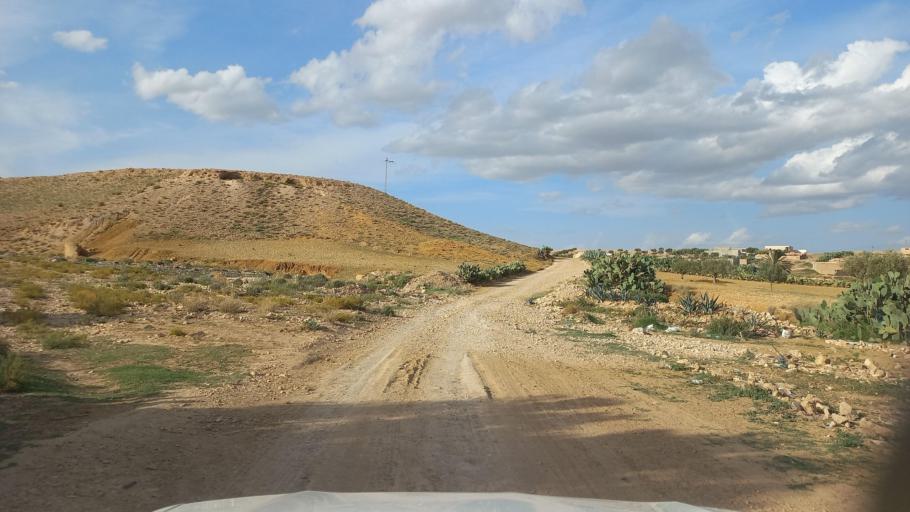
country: TN
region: Al Qasrayn
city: Sbiba
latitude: 35.4514
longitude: 9.0831
